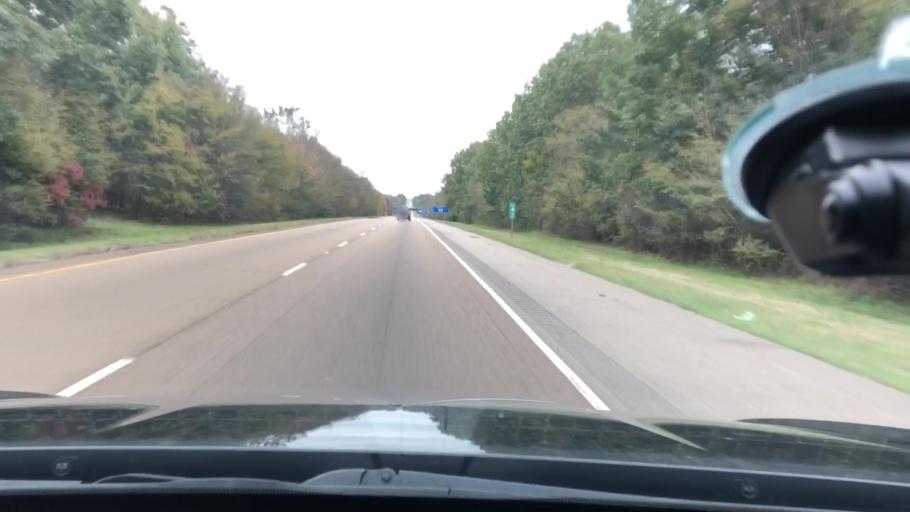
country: US
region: Arkansas
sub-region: Nevada County
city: Prescott
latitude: 33.7914
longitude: -93.4492
